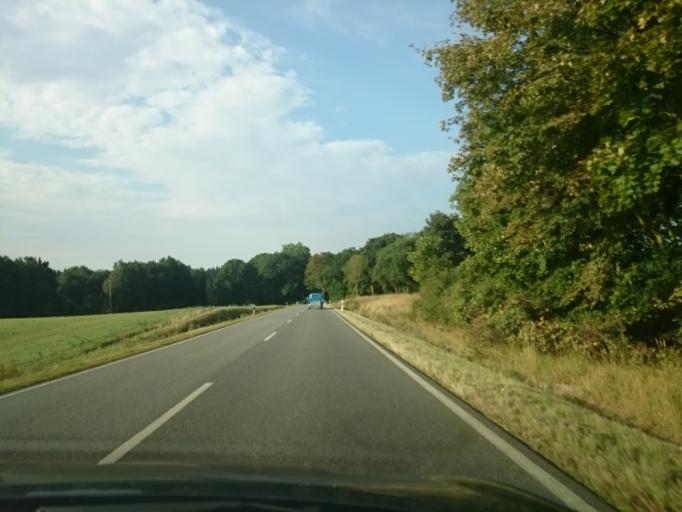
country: DE
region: Mecklenburg-Vorpommern
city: Demmin
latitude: 53.8688
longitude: 13.0148
